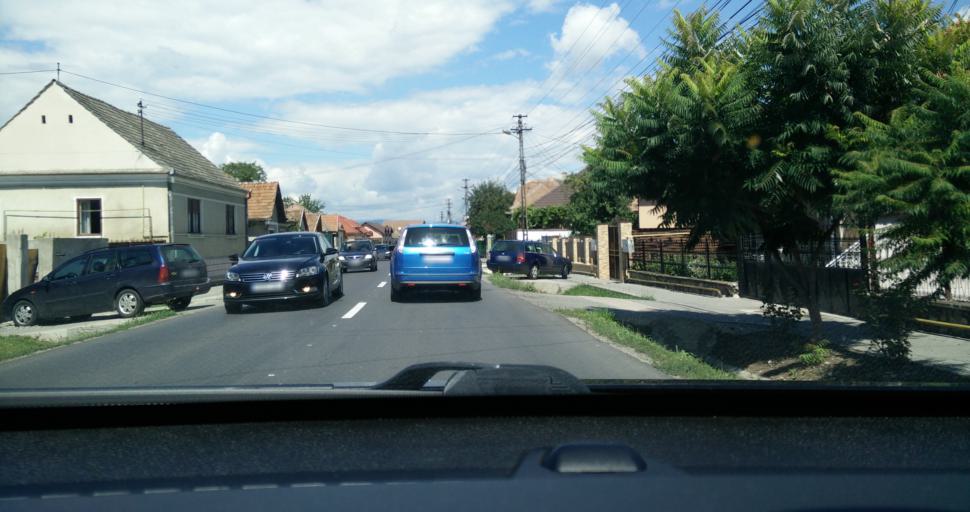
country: RO
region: Alba
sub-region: Municipiul Sebes
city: Petresti
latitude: 45.9251
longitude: 23.5620
